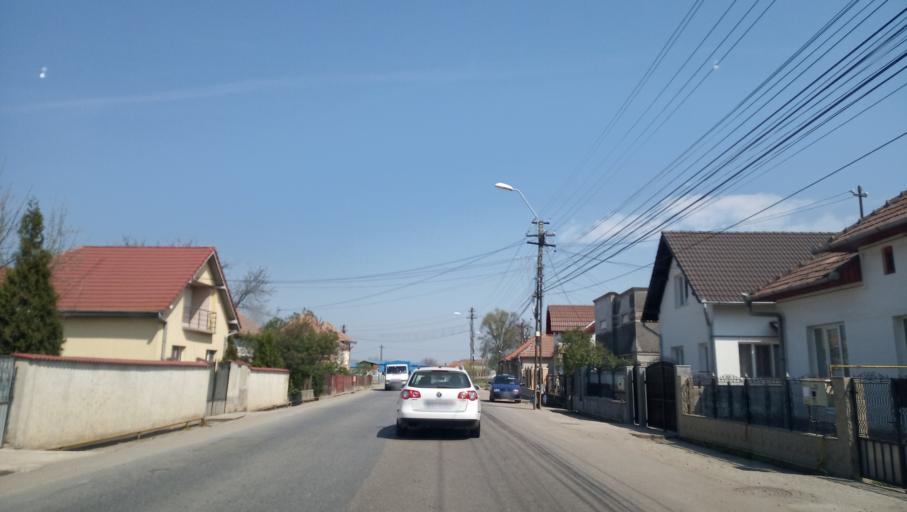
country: RO
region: Alba
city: Vurpar
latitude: 45.9956
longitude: 23.4872
